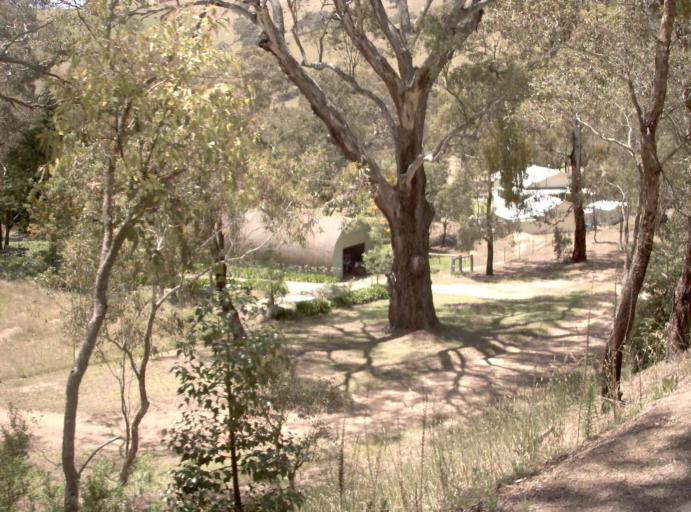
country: AU
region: Victoria
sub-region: East Gippsland
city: Bairnsdale
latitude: -37.3676
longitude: 147.8340
